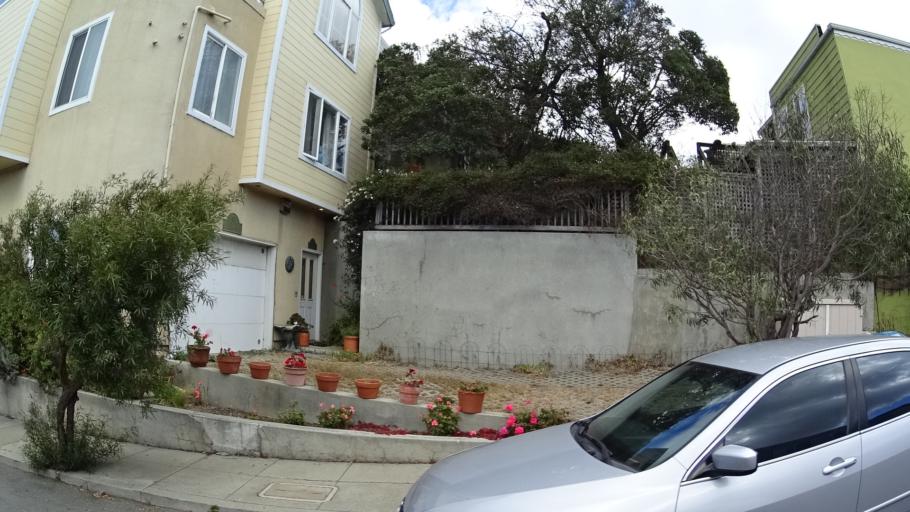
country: US
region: California
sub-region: San Francisco County
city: San Francisco
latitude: 37.7418
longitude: -122.4098
